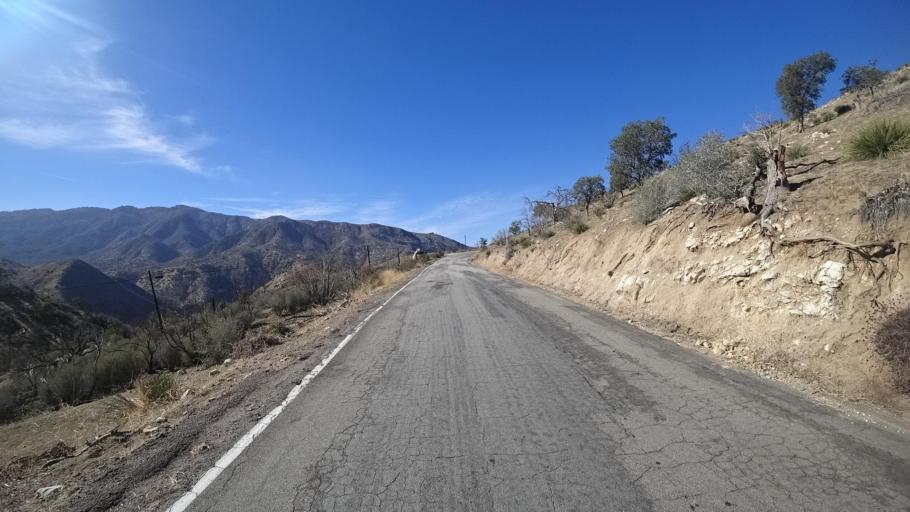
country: US
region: California
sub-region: Kern County
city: Bodfish
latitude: 35.5565
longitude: -118.5077
